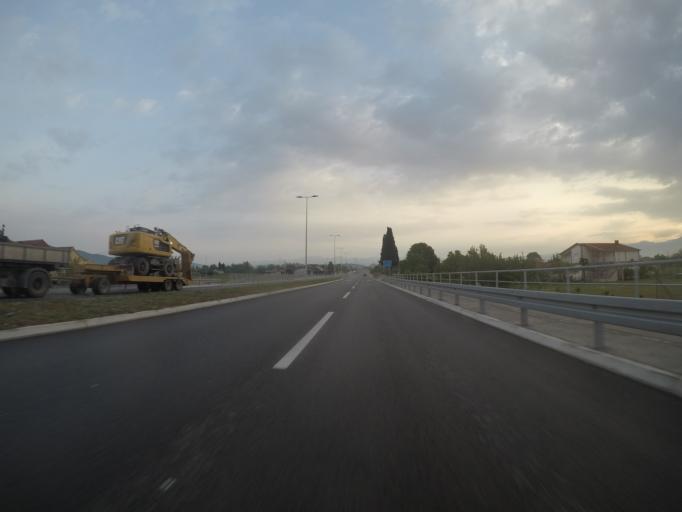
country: ME
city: Mojanovici
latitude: 42.3505
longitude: 19.2225
